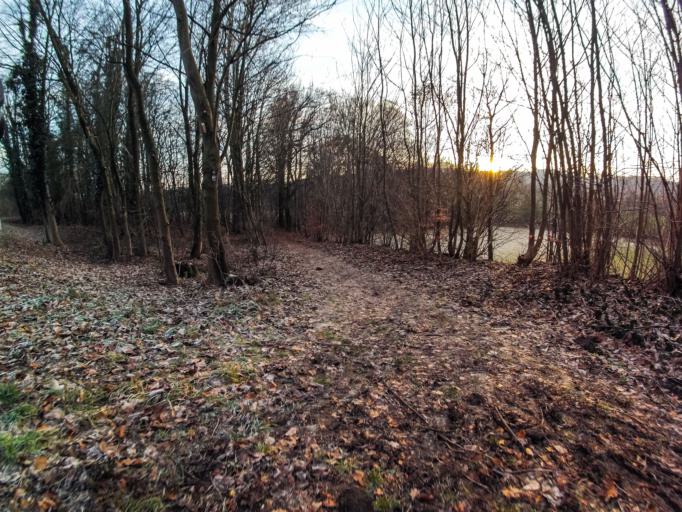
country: DE
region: North Rhine-Westphalia
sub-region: Regierungsbezirk Munster
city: Westerkappeln
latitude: 52.2888
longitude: 7.8366
